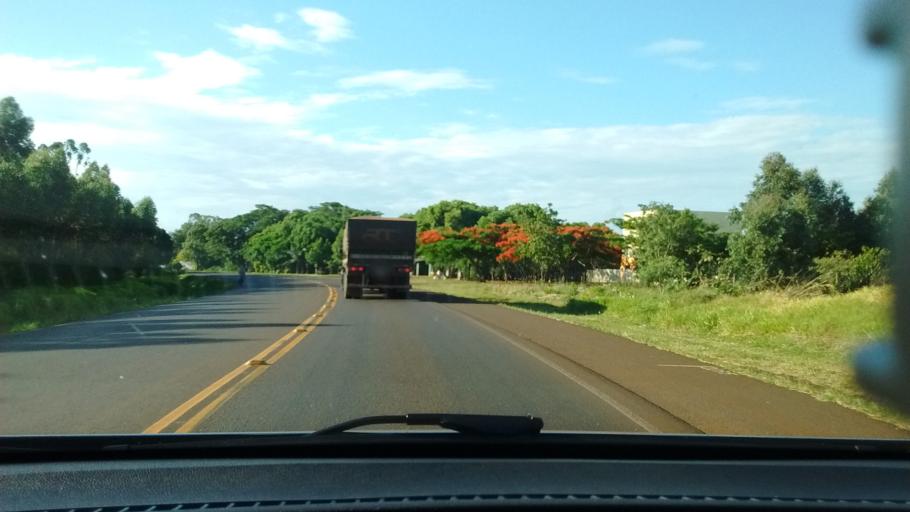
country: BR
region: Parana
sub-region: Cascavel
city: Cascavel
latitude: -25.2488
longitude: -53.5790
